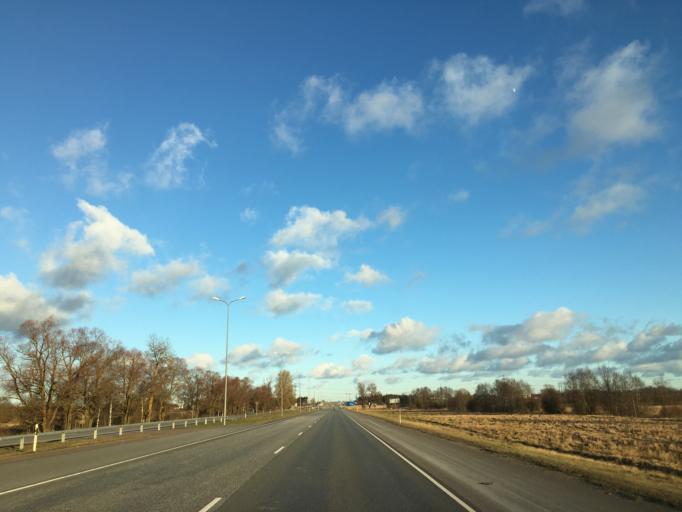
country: EE
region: Harju
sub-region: Saue vald
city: Laagri
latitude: 59.3276
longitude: 24.5960
